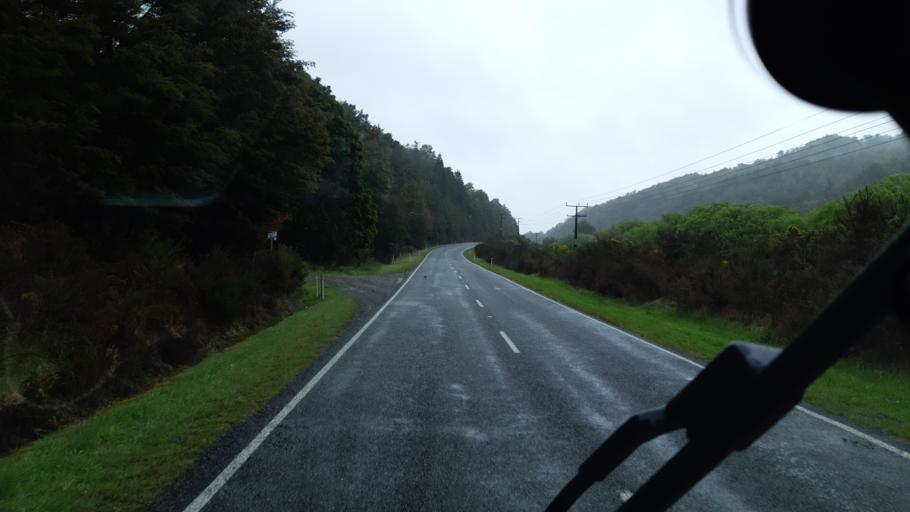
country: NZ
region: West Coast
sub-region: Buller District
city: Westport
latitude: -42.1480
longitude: 171.8039
